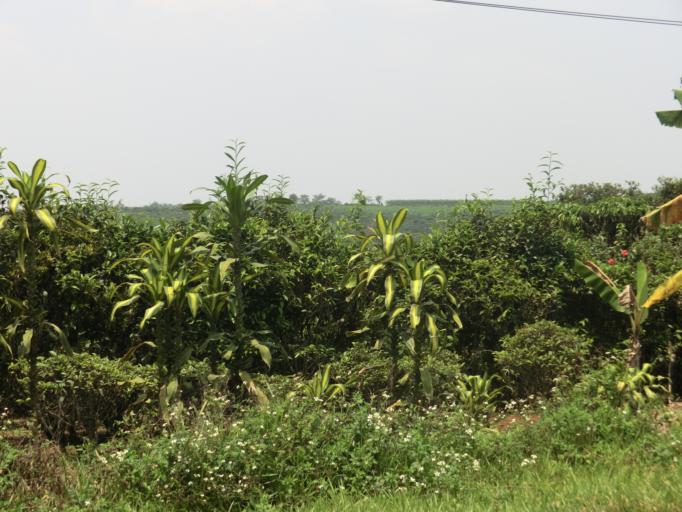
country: VN
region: Lam Dong
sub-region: Thanh Pho Bao Loc
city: Bao Loc
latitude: 11.5811
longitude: 107.8029
